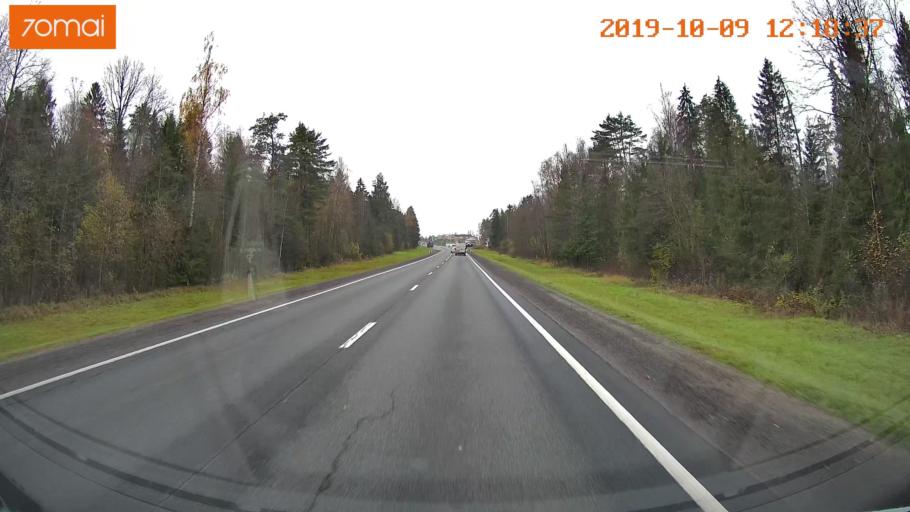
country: RU
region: Jaroslavl
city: Prechistoye
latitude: 58.4398
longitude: 40.3213
